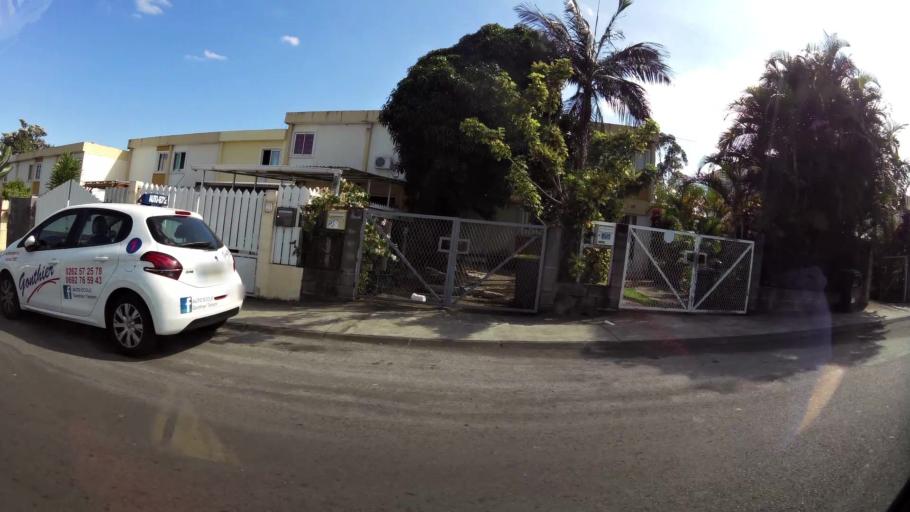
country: RE
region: Reunion
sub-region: Reunion
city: Le Tampon
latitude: -21.2865
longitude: 55.5103
